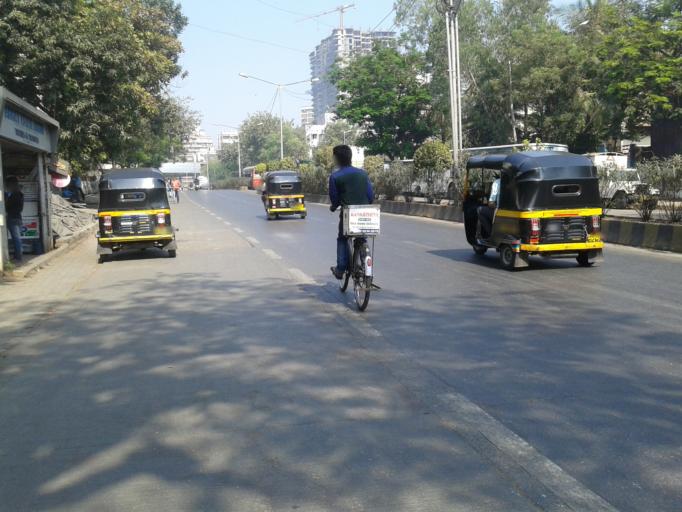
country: IN
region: Maharashtra
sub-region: Mumbai Suburban
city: Borivli
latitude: 19.2474
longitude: 72.8619
